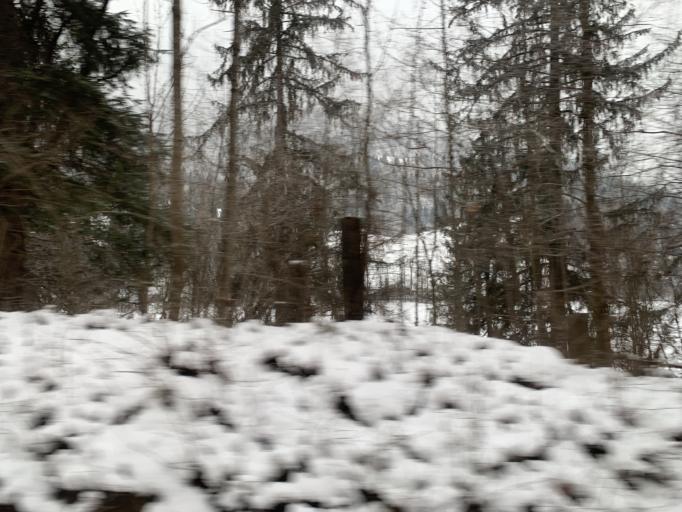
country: DE
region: Bavaria
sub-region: Upper Bavaria
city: Garmisch-Partenkirchen
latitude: 47.4848
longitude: 11.1338
